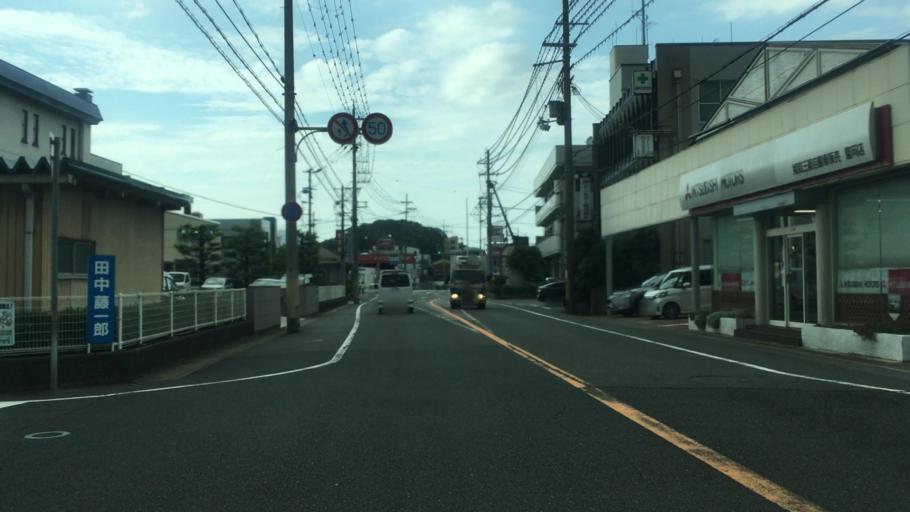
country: JP
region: Hyogo
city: Toyooka
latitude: 35.5302
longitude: 134.8200
